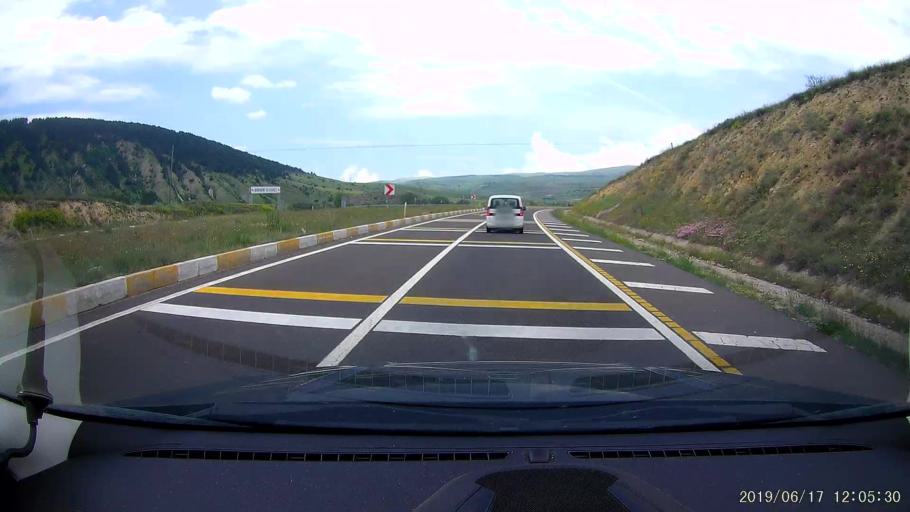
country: TR
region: Cankiri
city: Cerkes
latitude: 40.8316
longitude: 32.7762
